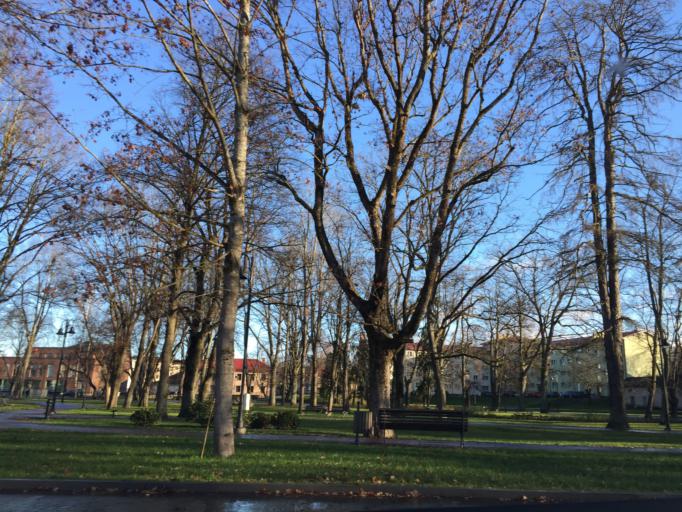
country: LV
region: Valmieras Rajons
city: Valmiera
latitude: 57.5369
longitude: 25.4168
